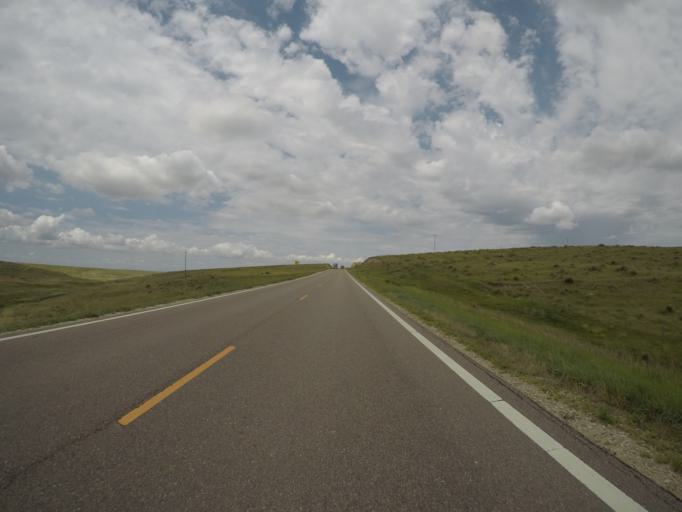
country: US
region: Kansas
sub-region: Rawlins County
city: Atwood
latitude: 39.7406
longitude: -101.0526
